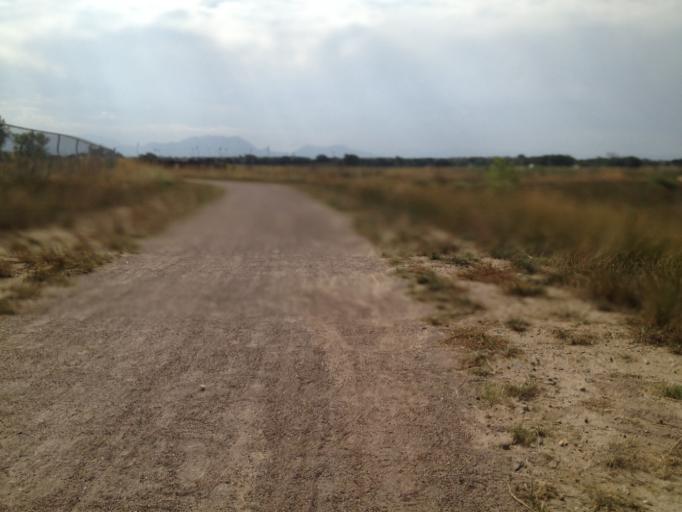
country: US
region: Colorado
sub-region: Boulder County
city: Louisville
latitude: 39.9831
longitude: -105.1168
